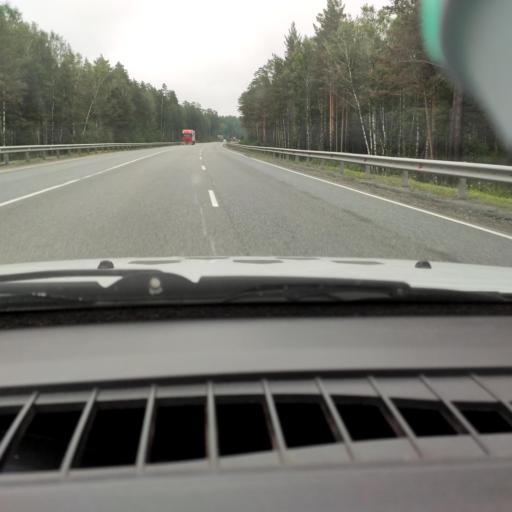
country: RU
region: Chelyabinsk
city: Zlatoust
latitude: 55.0554
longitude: 59.7033
